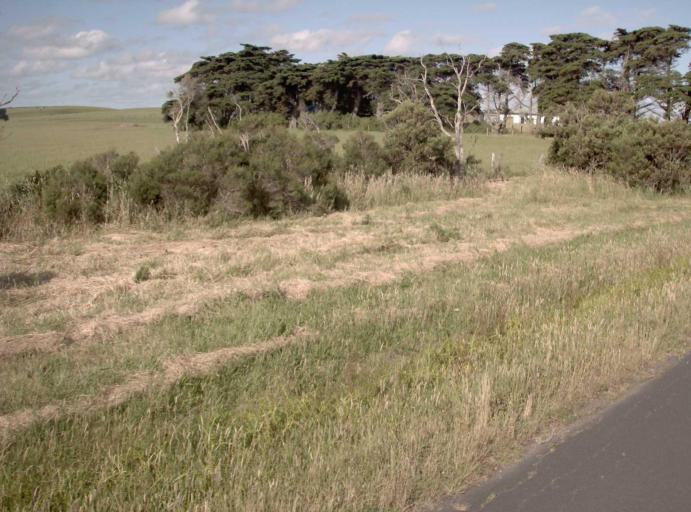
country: AU
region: Victoria
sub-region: Bass Coast
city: North Wonthaggi
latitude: -38.5622
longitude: 145.5259
